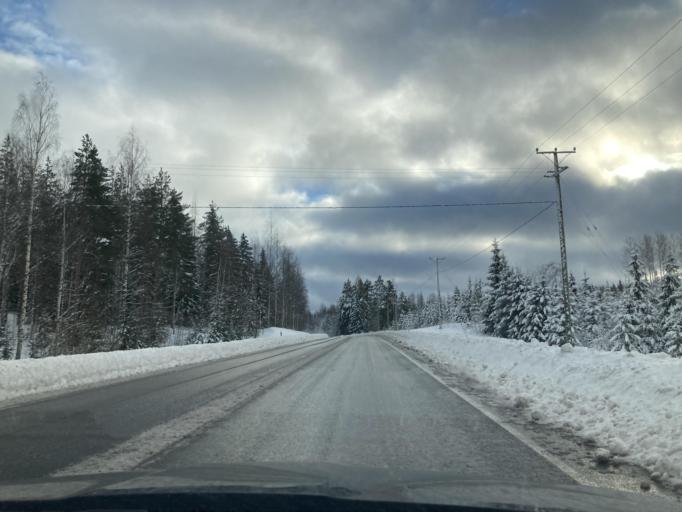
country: FI
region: Central Finland
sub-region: Jaemsae
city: Jaemsae
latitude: 61.7742
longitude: 25.2287
